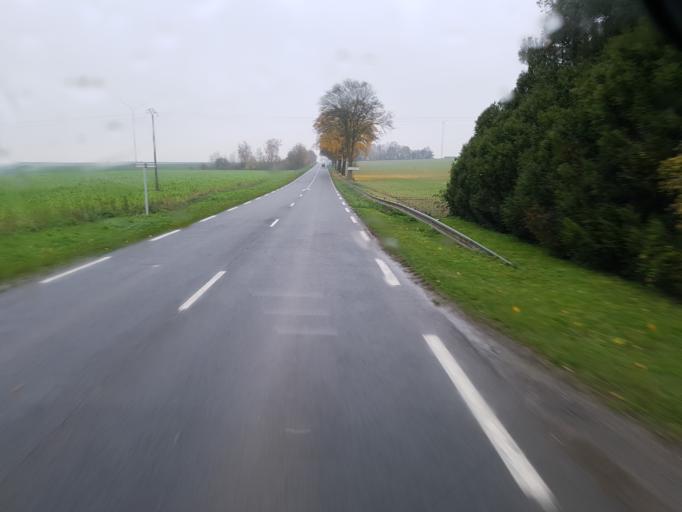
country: FR
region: Picardie
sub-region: Departement de l'Aisne
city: Saint-Quentin
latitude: 49.8942
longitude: 3.2640
